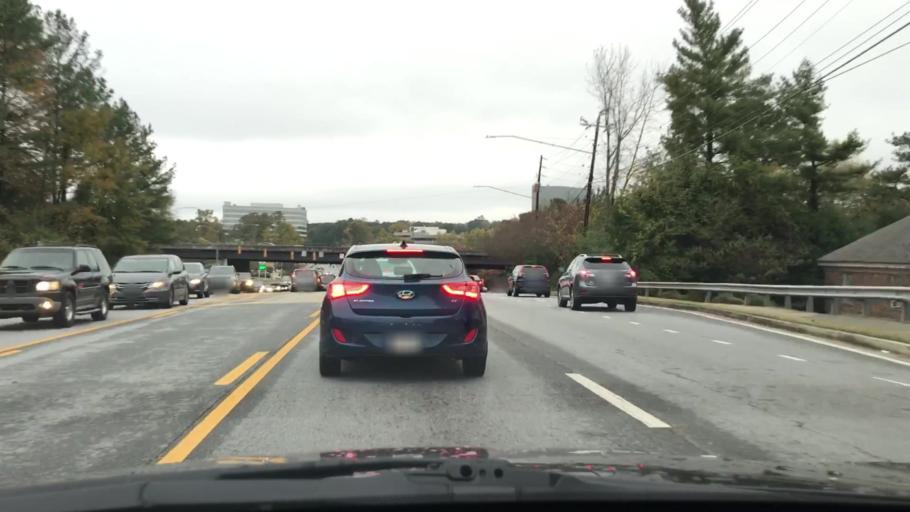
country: US
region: Georgia
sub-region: DeKalb County
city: North Druid Hills
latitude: 33.8389
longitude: -84.3124
